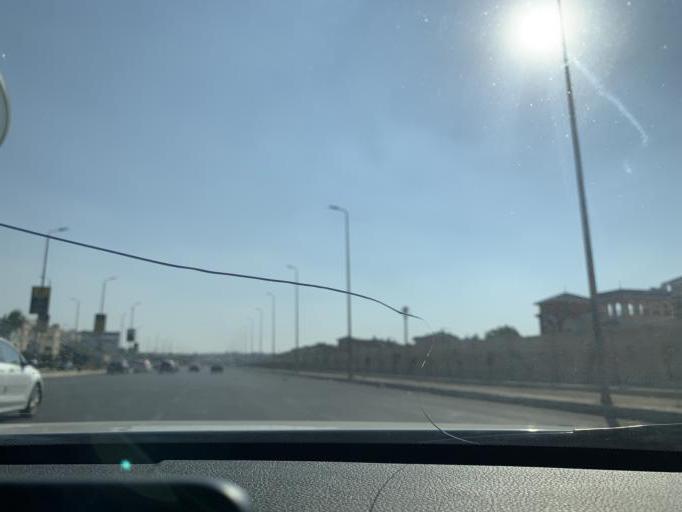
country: EG
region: Muhafazat al Qalyubiyah
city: Al Khankah
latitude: 30.0176
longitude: 31.4747
